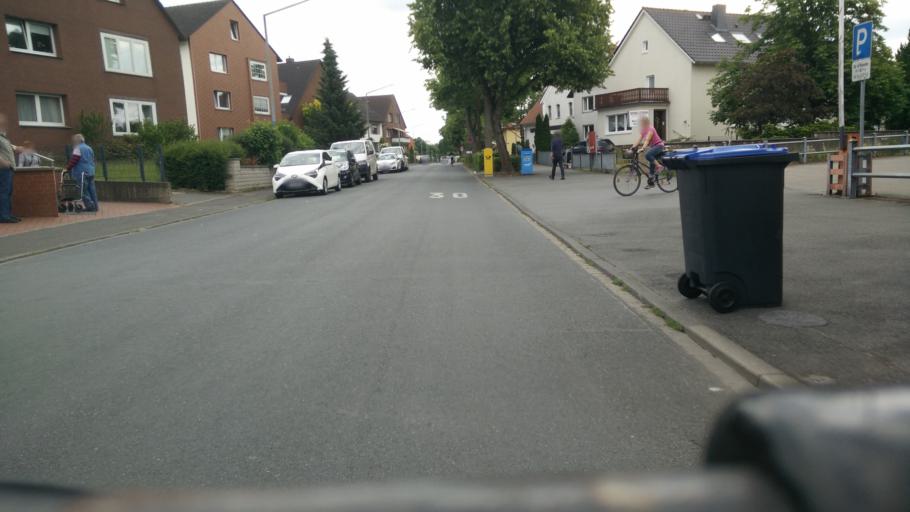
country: DE
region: Lower Saxony
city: Wunstorf
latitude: 52.4269
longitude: 9.4726
